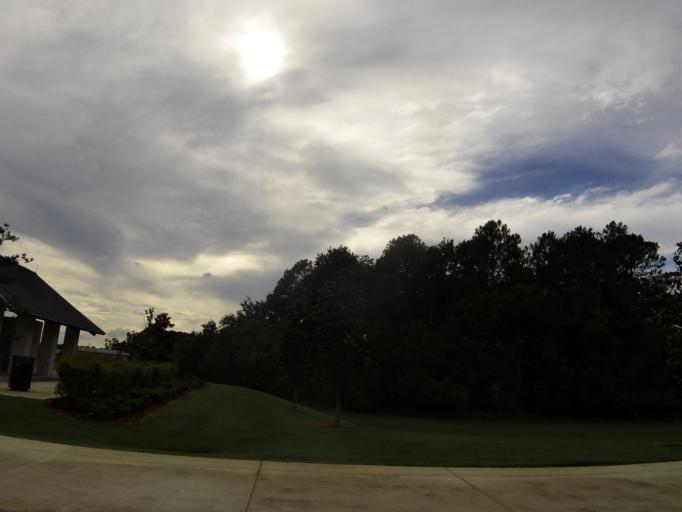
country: US
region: Florida
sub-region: Nassau County
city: Nassau Village-Ratliff
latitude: 30.5483
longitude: -81.7210
